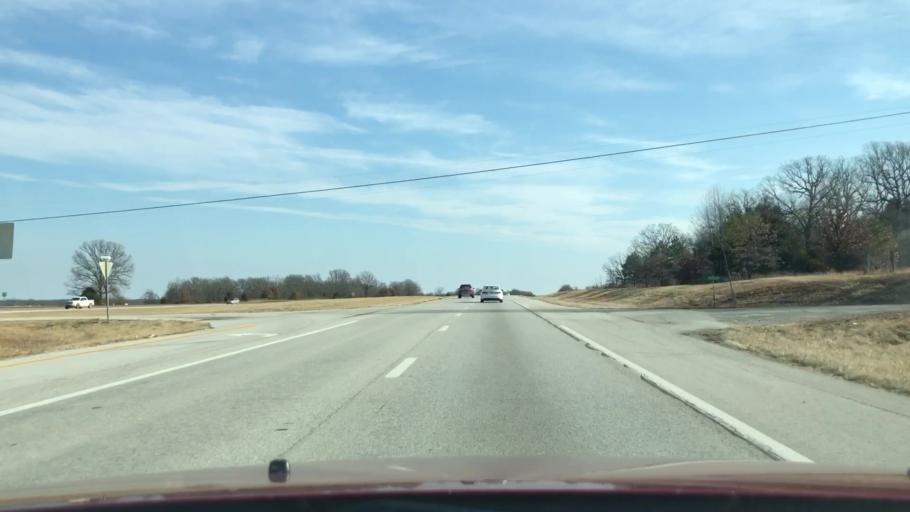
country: US
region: Missouri
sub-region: Webster County
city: Rogersville
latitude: 37.1214
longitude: -93.0024
